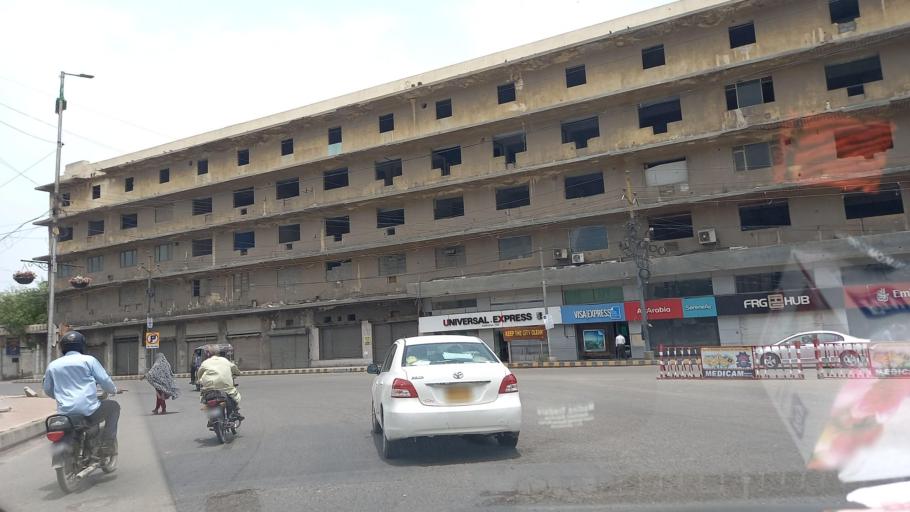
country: PK
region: Sindh
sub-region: Karachi District
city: Karachi
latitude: 24.8511
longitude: 67.0299
